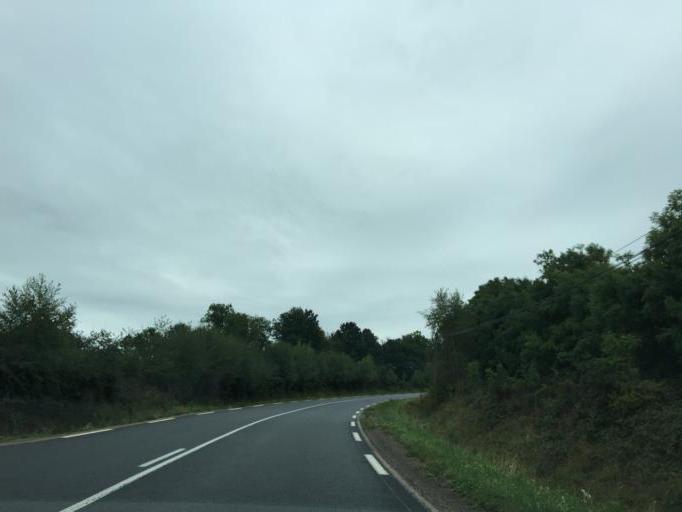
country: FR
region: Midi-Pyrenees
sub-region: Departement de l'Aveyron
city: Espalion
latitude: 44.5945
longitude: 2.7972
